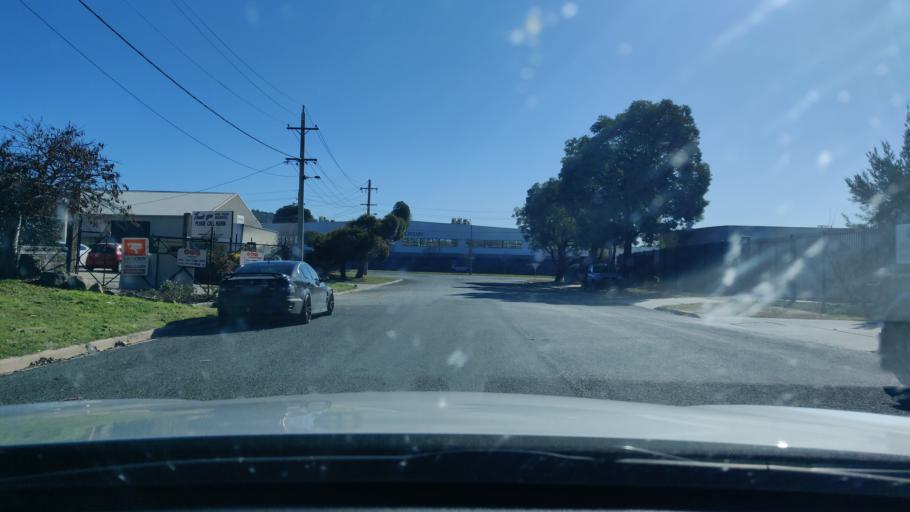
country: AU
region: Australian Capital Territory
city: Macarthur
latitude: -35.3890
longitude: 149.1717
